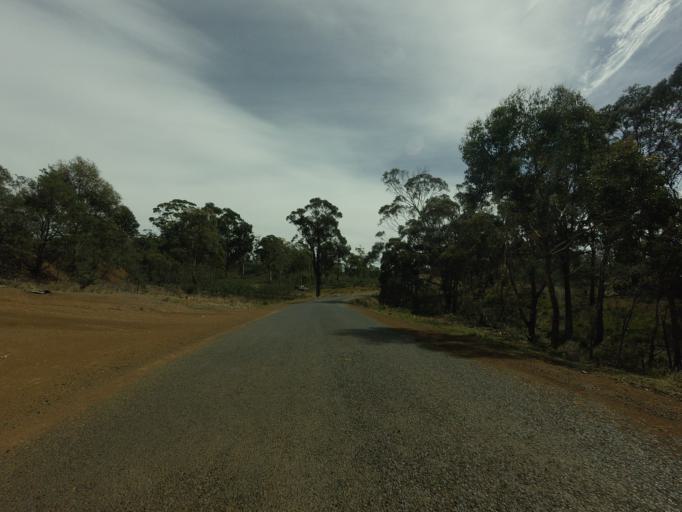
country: AU
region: Tasmania
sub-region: Sorell
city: Sorell
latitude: -42.5592
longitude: 147.6797
